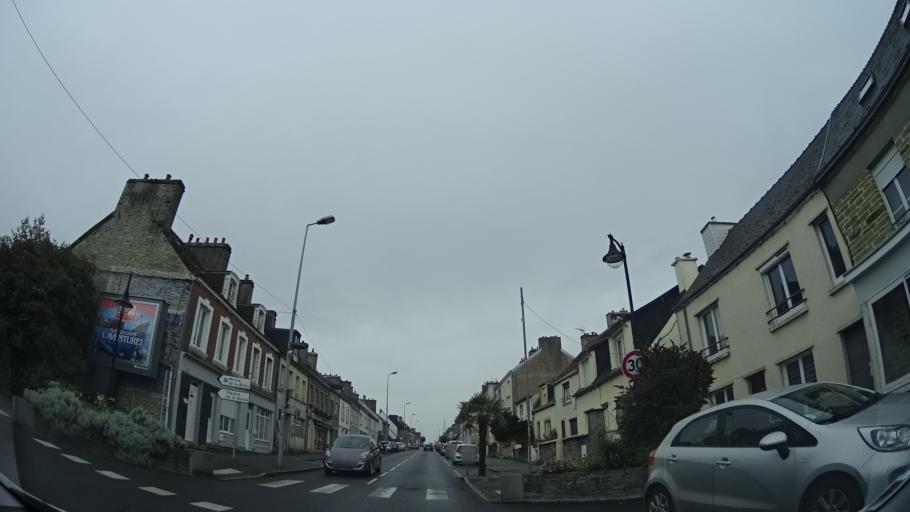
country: FR
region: Lower Normandy
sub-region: Departement de la Manche
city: Octeville
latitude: 49.6274
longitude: -1.6427
